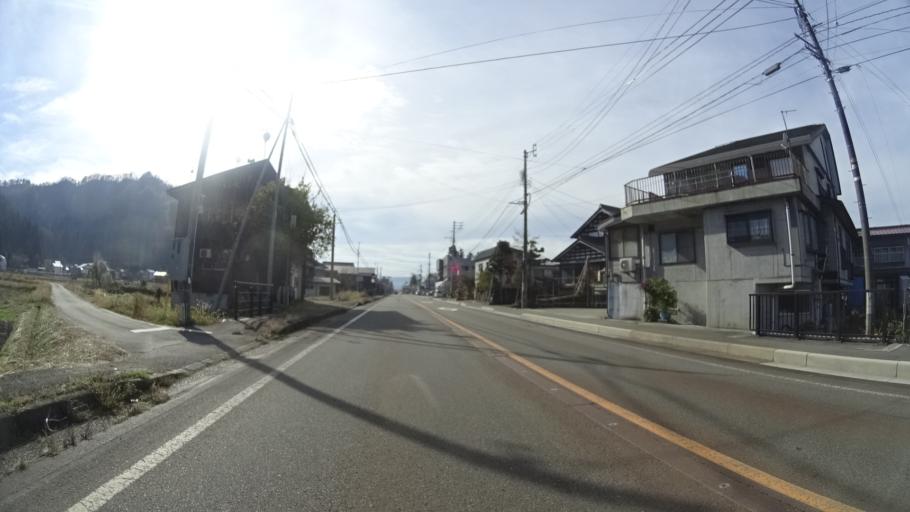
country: JP
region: Niigata
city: Muikamachi
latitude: 37.1236
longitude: 138.9290
